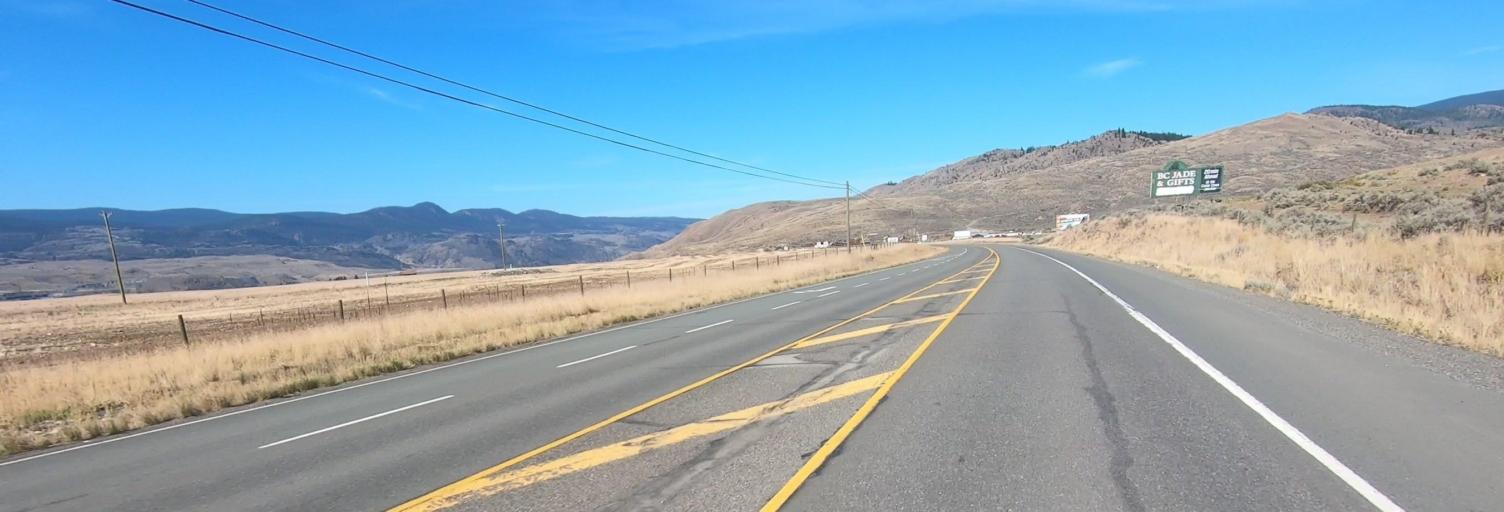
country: CA
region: British Columbia
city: Logan Lake
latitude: 50.7714
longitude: -120.9415
